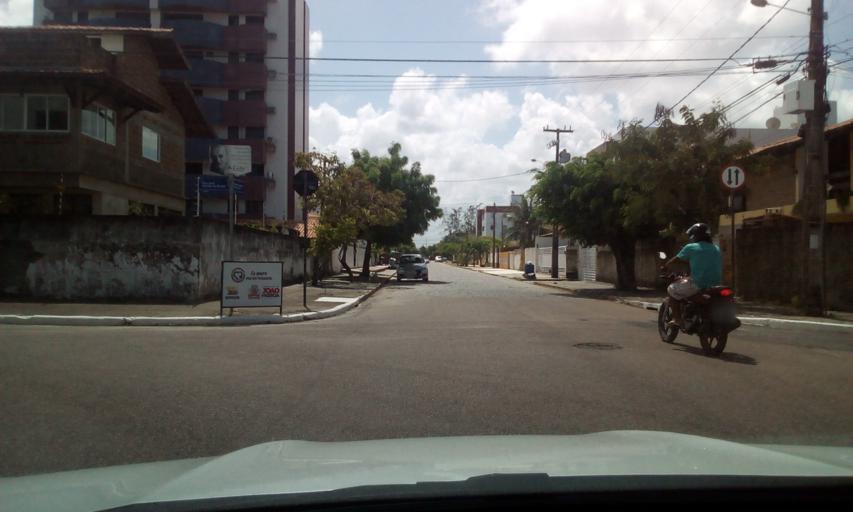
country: BR
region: Paraiba
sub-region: Joao Pessoa
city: Joao Pessoa
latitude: -7.0690
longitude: -34.8394
